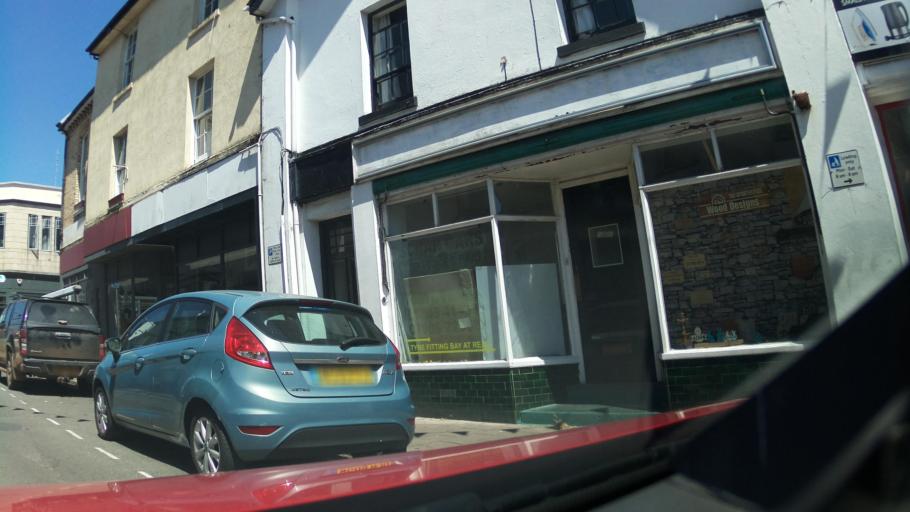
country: GB
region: England
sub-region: Borough of Torbay
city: Paignton
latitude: 50.4351
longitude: -3.5716
